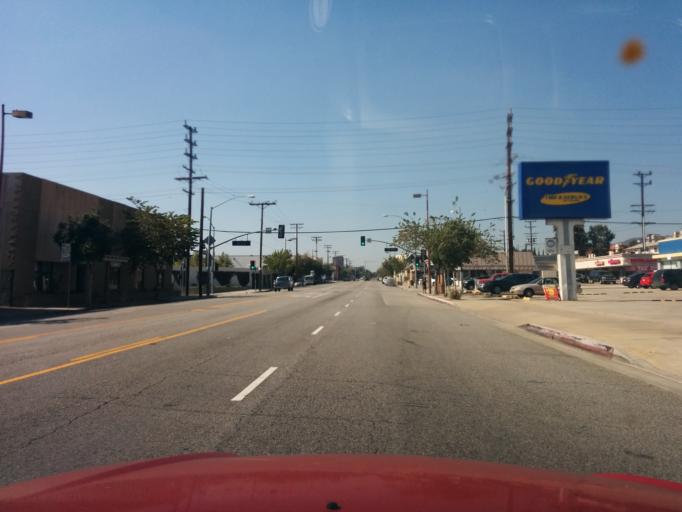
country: US
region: California
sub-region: Los Angeles County
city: Burbank
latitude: 34.1712
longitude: -118.2953
